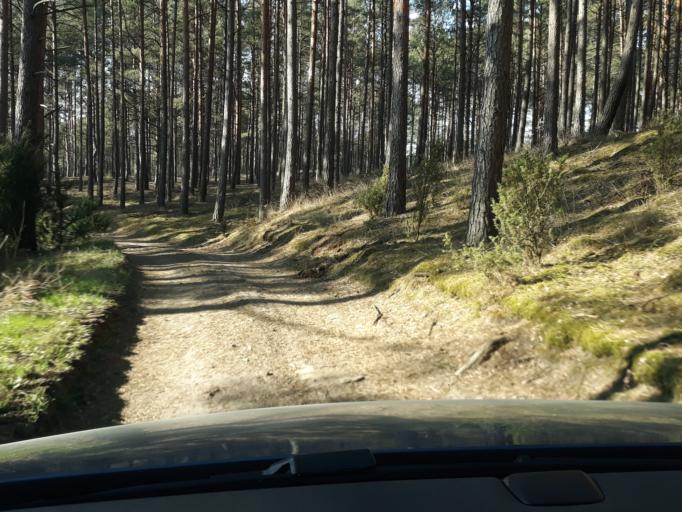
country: PL
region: Pomeranian Voivodeship
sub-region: Powiat bytowski
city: Lipnica
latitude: 53.8972
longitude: 17.4153
